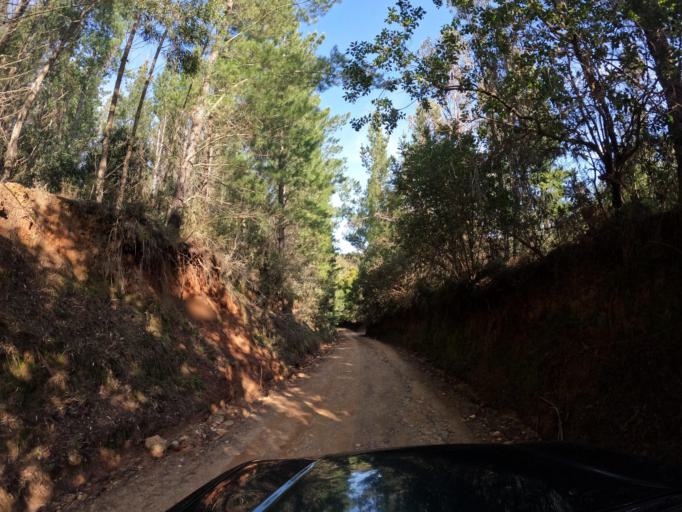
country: CL
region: Biobio
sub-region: Provincia de Biobio
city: La Laja
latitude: -37.1288
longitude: -72.7347
